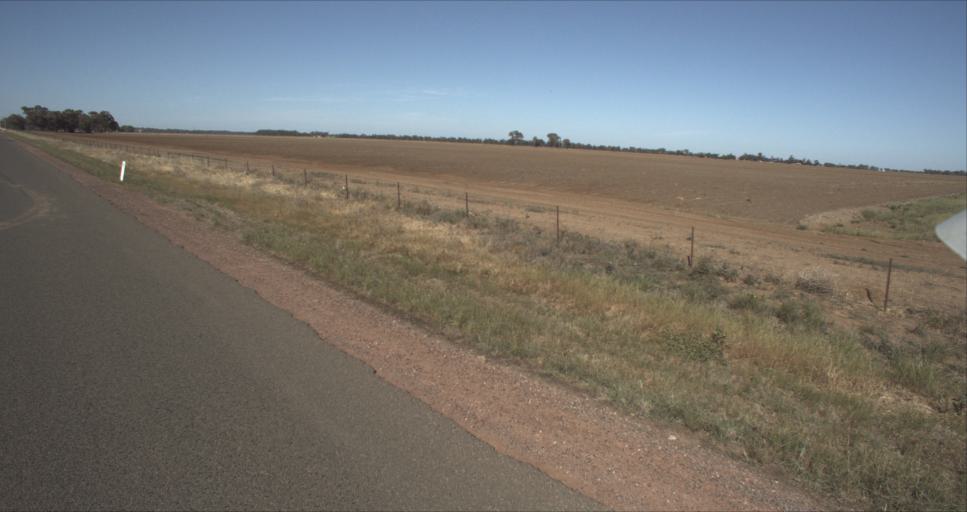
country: AU
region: New South Wales
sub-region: Leeton
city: Leeton
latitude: -34.5721
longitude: 146.2633
